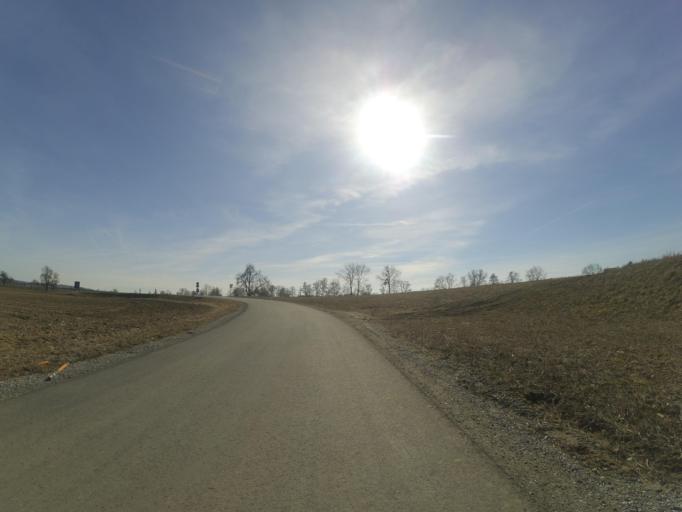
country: DE
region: Baden-Wuerttemberg
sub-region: Tuebingen Region
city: Meckenbeuren
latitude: 47.7395
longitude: 9.5816
